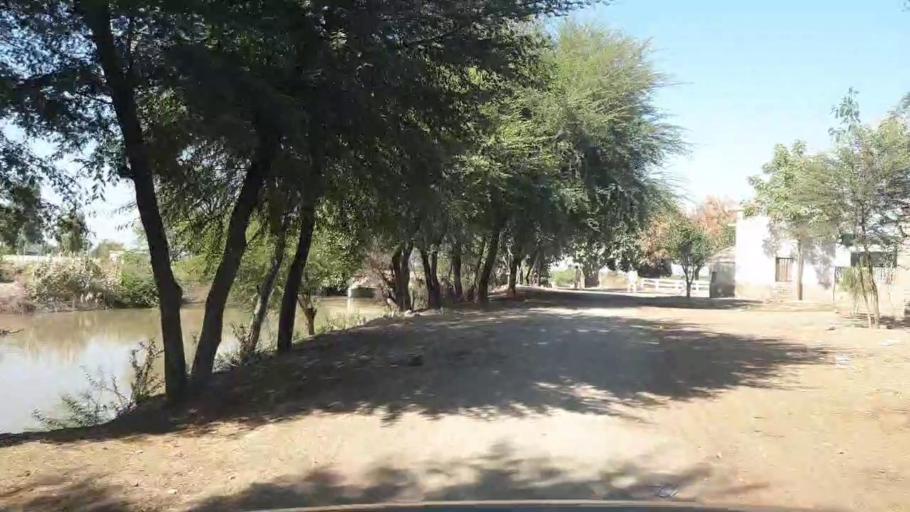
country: PK
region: Sindh
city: Dhoro Naro
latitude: 25.4014
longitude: 69.6142
